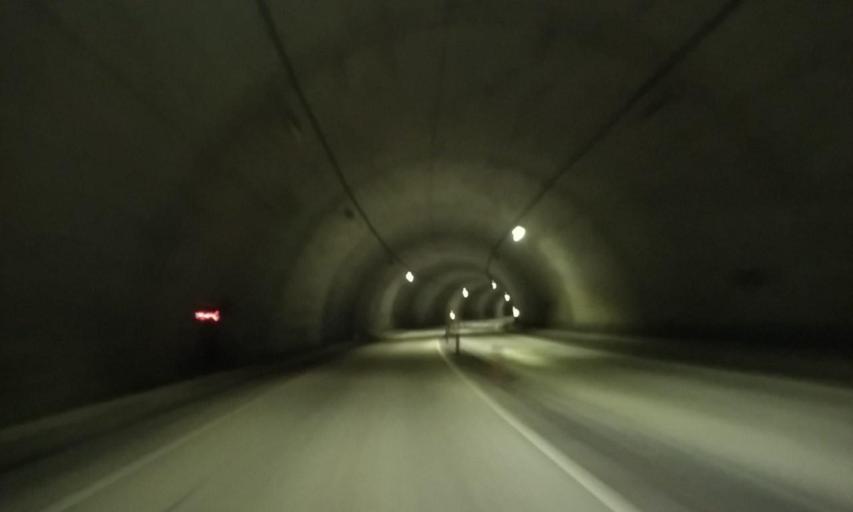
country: JP
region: Wakayama
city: Shingu
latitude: 33.7195
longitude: 135.9781
